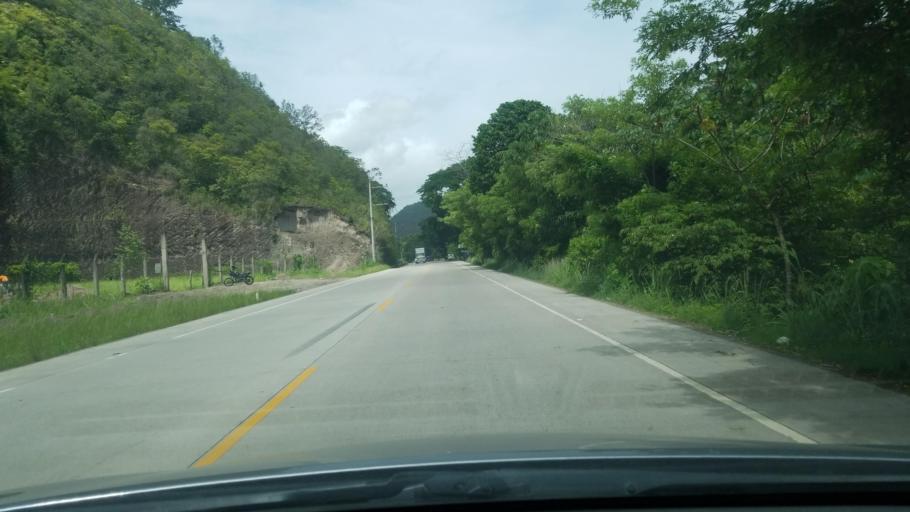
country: HN
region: Copan
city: La Entrada
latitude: 15.0464
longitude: -88.7616
